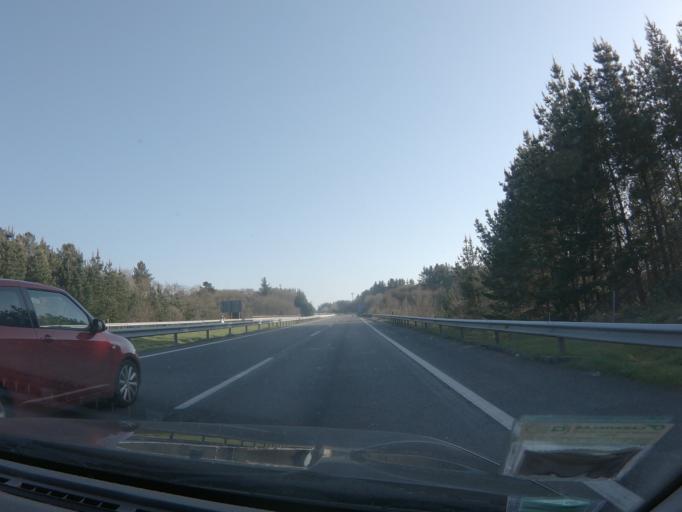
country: ES
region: Galicia
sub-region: Provincia de Lugo
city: Lugo
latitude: 43.0306
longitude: -7.5218
